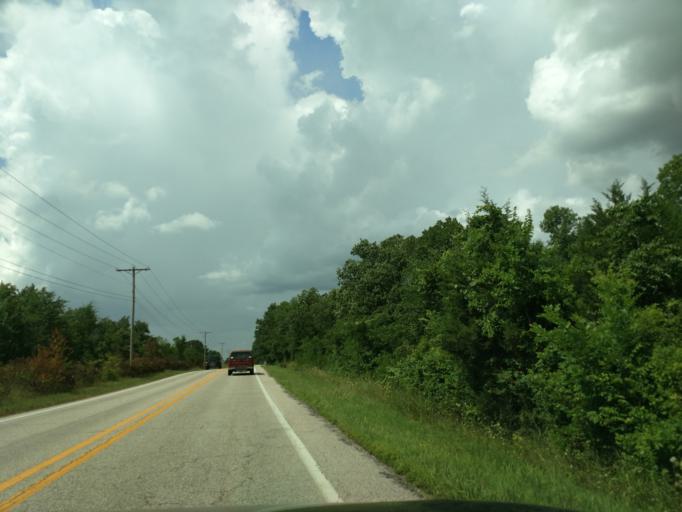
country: US
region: Arkansas
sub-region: Boone County
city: Harrison
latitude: 36.2819
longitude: -93.2353
